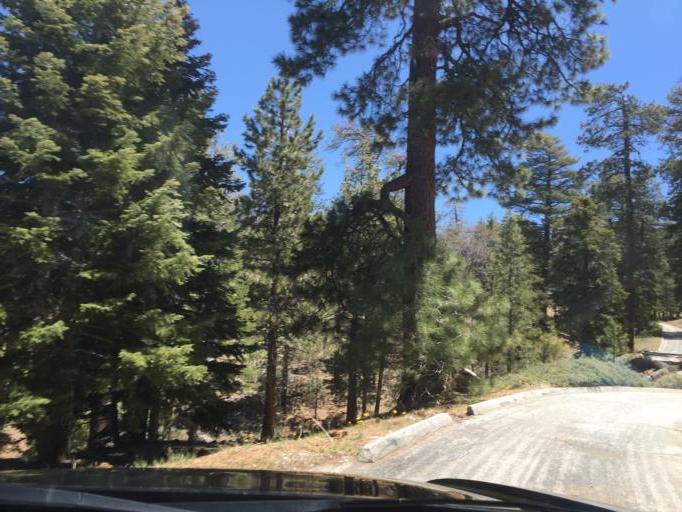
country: US
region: California
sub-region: San Bernardino County
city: Pinon Hills
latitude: 34.3898
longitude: -117.6959
